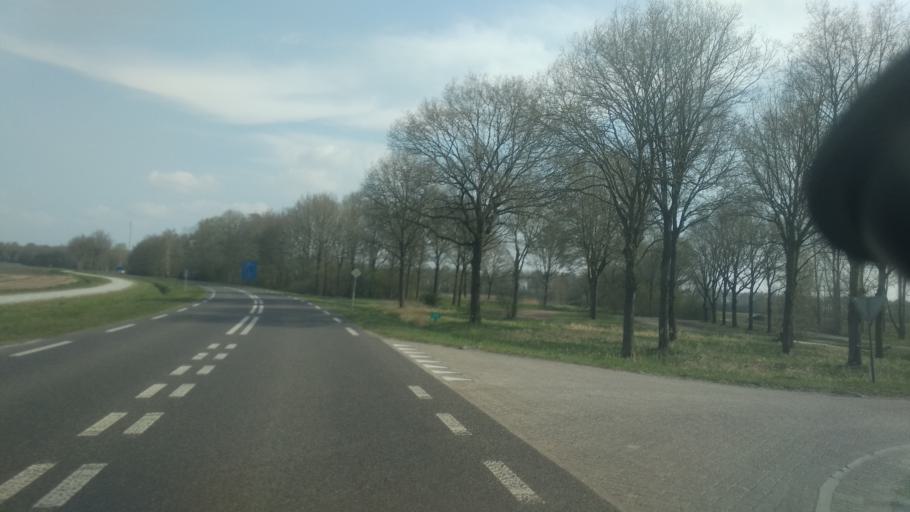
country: NL
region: Groningen
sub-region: Gemeente Stadskanaal
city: Stadskanaal
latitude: 52.9658
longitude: 6.8894
